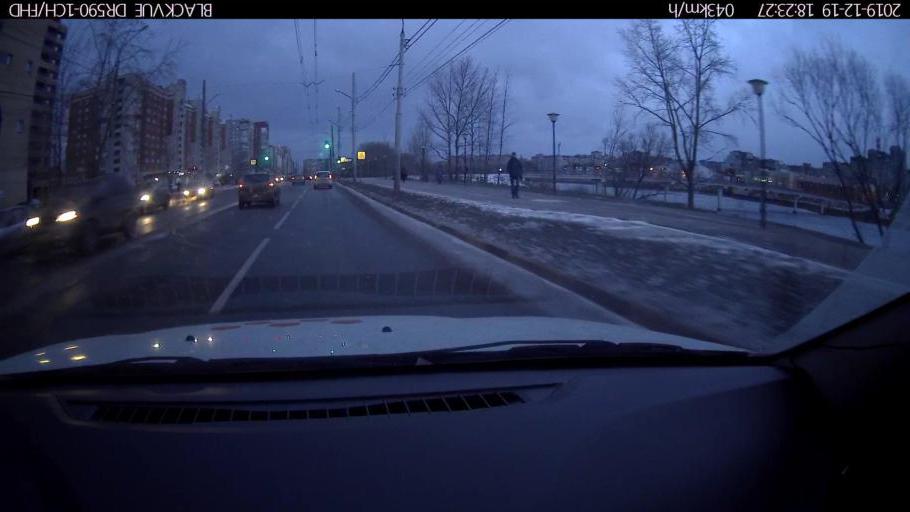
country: RU
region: Nizjnij Novgorod
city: Nizhniy Novgorod
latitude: 56.3356
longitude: 43.9425
